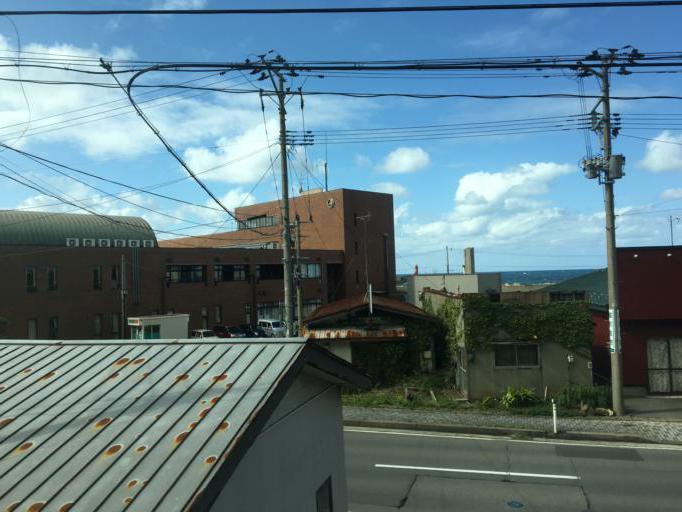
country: JP
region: Akita
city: Noshiromachi
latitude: 40.6480
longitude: 139.9284
